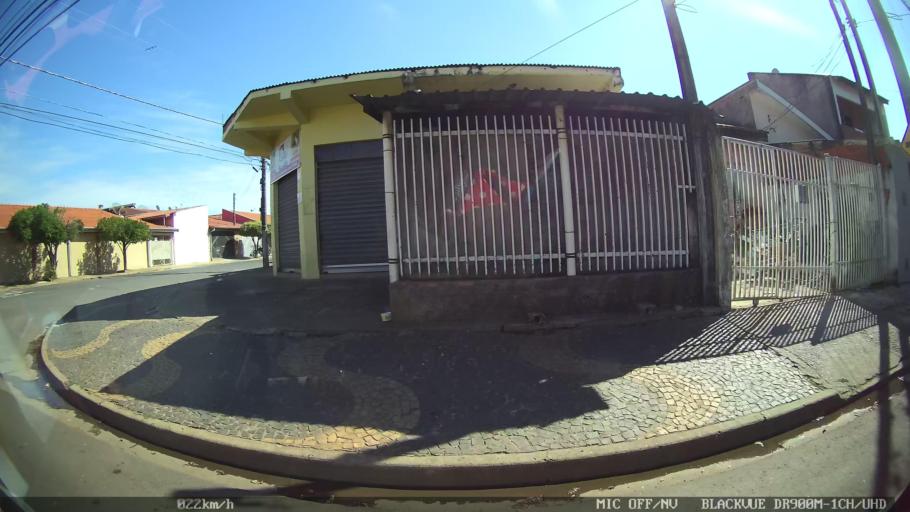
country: BR
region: Sao Paulo
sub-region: Santa Barbara D'Oeste
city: Santa Barbara d'Oeste
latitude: -22.7372
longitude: -47.4114
